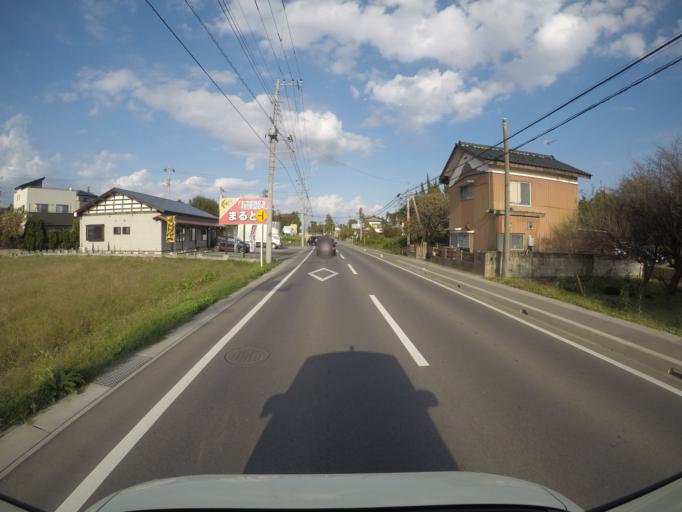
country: JP
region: Ibaraki
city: Mitsukaido
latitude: 36.0010
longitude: 140.0483
